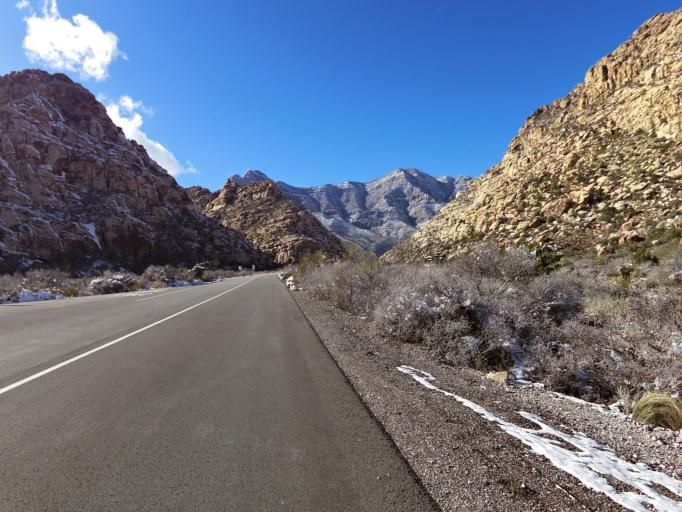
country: US
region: Nevada
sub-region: Clark County
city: Summerlin South
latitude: 36.1575
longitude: -115.4936
